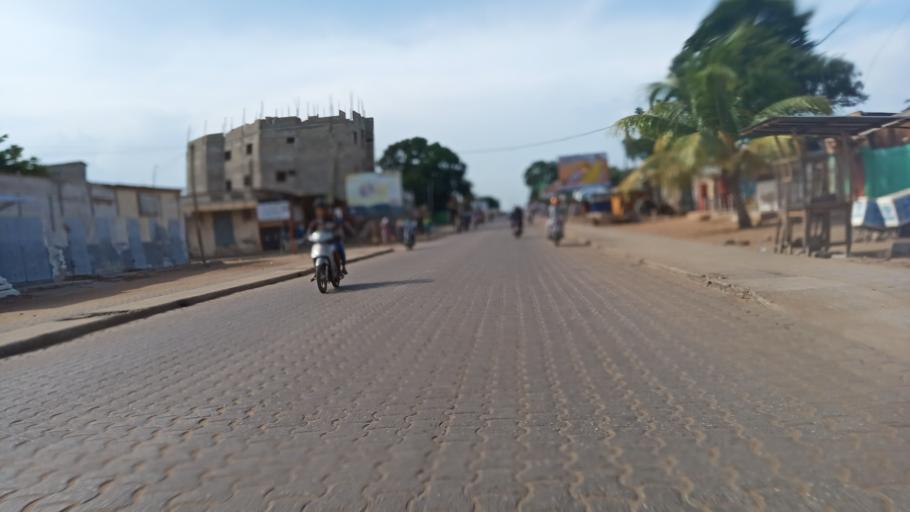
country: TG
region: Maritime
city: Lome
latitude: 6.1590
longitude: 1.2661
